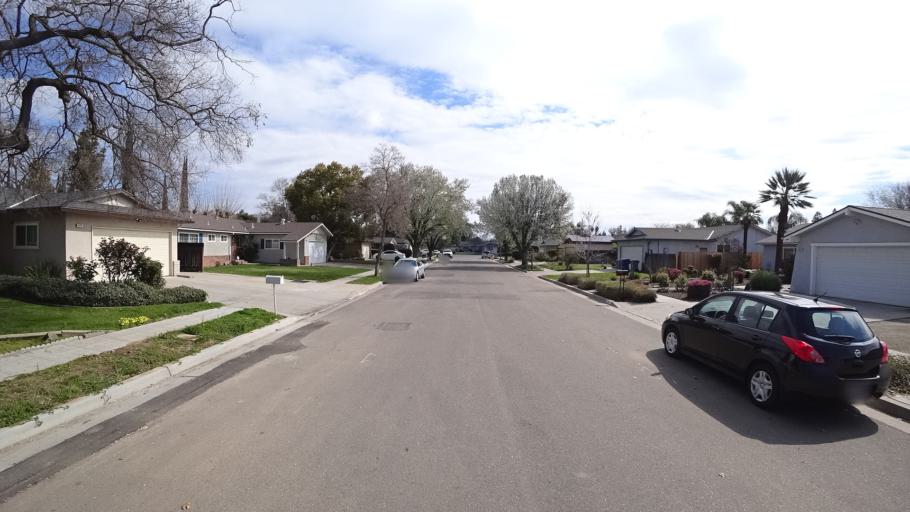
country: US
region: California
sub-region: Fresno County
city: Fresno
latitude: 36.8183
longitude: -119.8530
